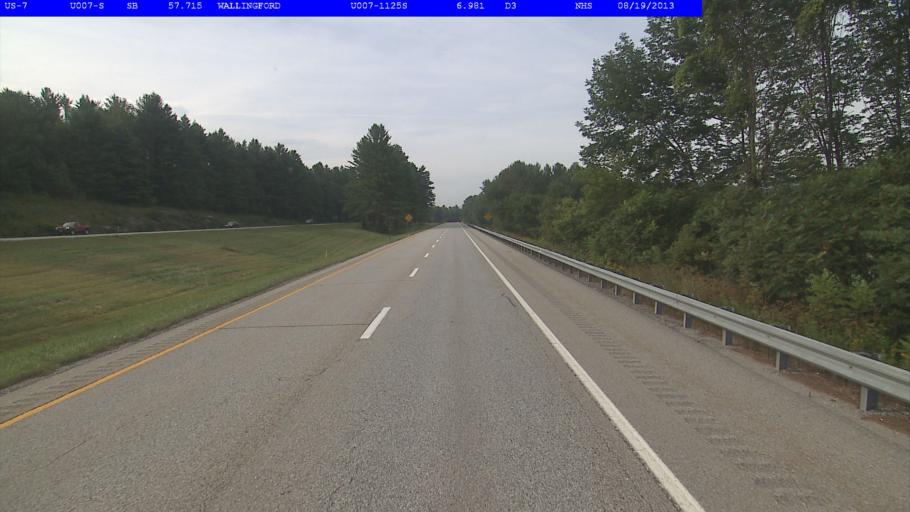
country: US
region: Vermont
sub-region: Rutland County
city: Rutland
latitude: 43.4932
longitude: -72.9700
